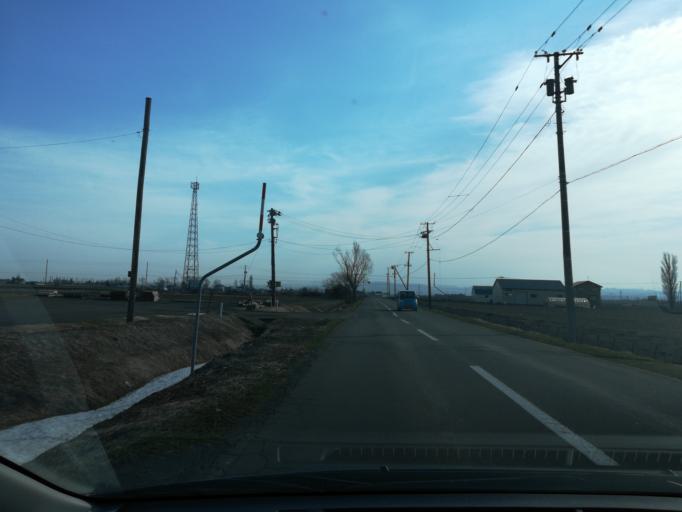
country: JP
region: Hokkaido
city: Iwamizawa
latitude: 43.1942
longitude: 141.7145
